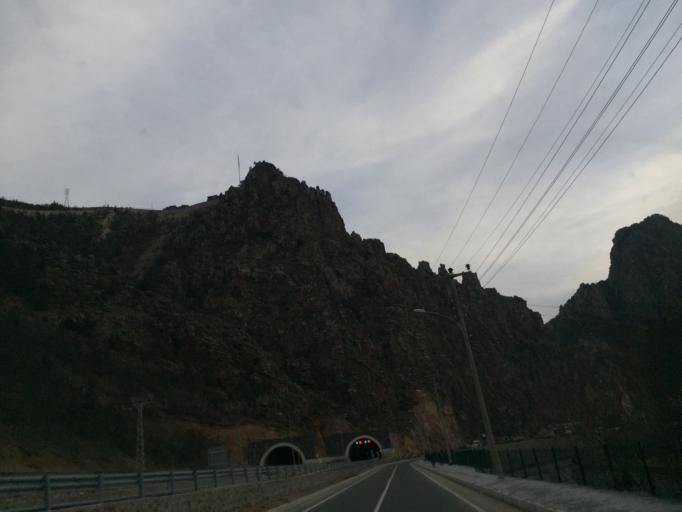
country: TR
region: Gumushane
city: Torul
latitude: 40.5603
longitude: 39.2977
